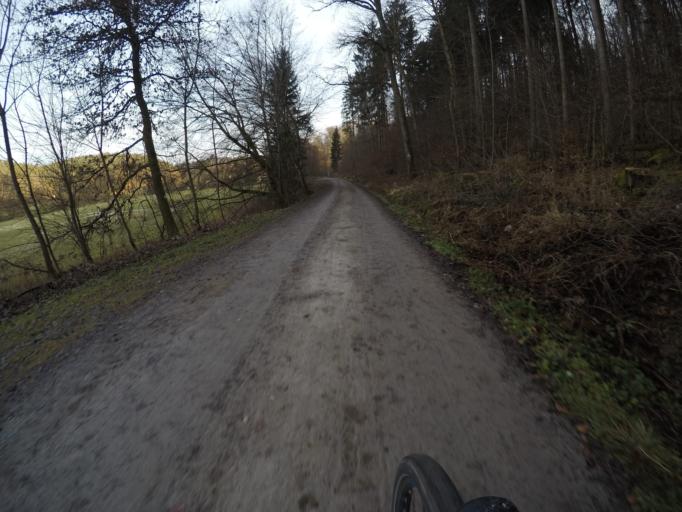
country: DE
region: Baden-Wuerttemberg
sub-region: Regierungsbezirk Stuttgart
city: Waldenbuch
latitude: 48.6434
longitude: 9.1090
